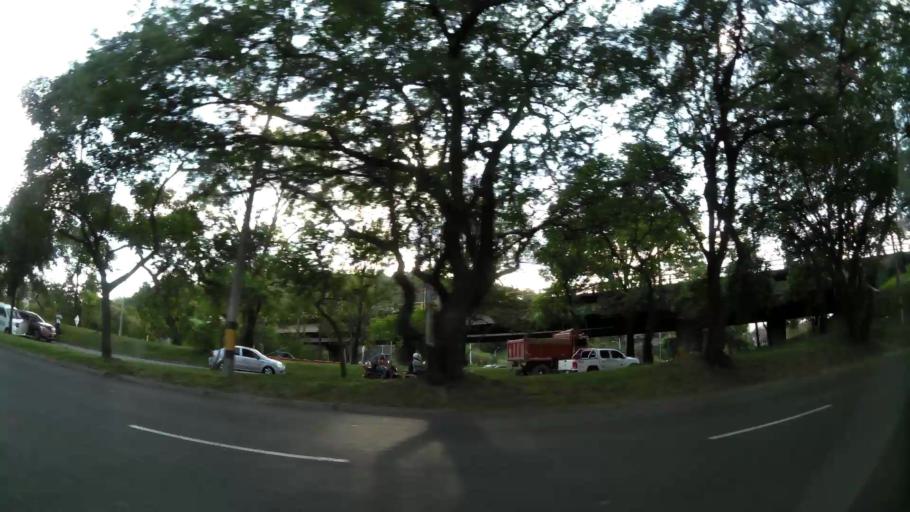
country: CO
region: Antioquia
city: Medellin
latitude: 6.2371
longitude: -75.5758
